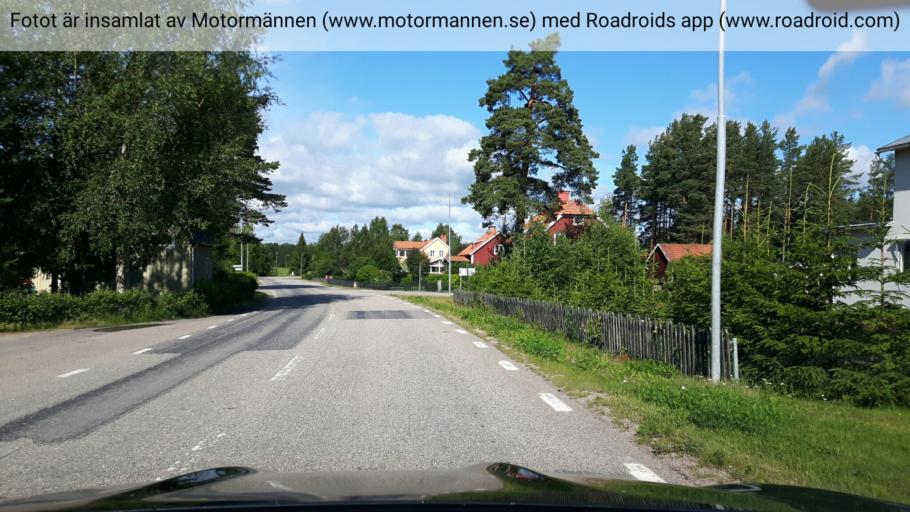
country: SE
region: Gaevleborg
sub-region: Ljusdals Kommun
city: Farila
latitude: 61.8108
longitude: 15.7544
